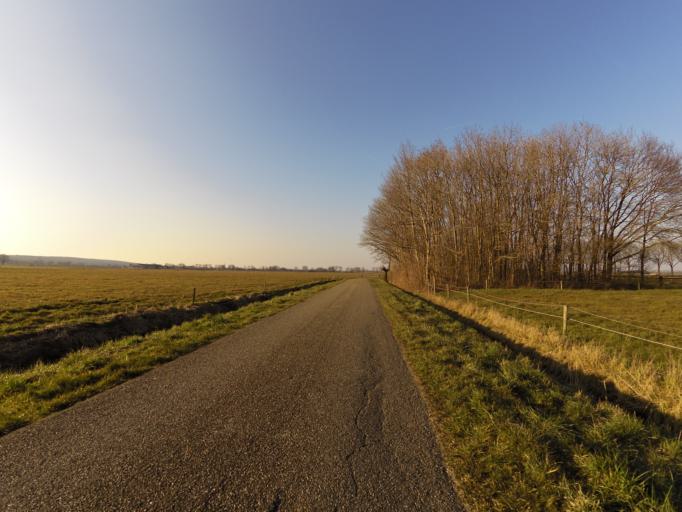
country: NL
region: Gelderland
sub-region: Gemeente Montferland
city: s-Heerenberg
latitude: 51.9005
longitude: 6.2845
